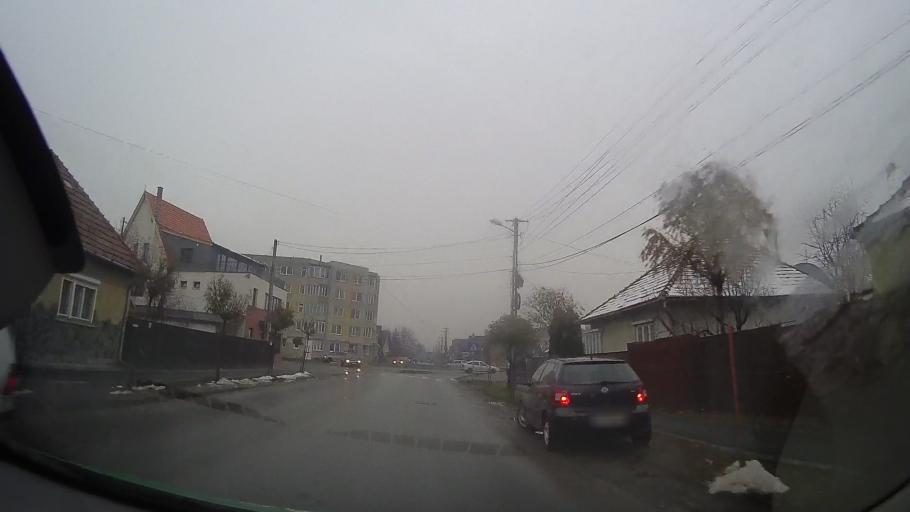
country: RO
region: Harghita
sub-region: Municipiul Gheorgheni
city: Gheorgheni
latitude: 46.7226
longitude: 25.5898
